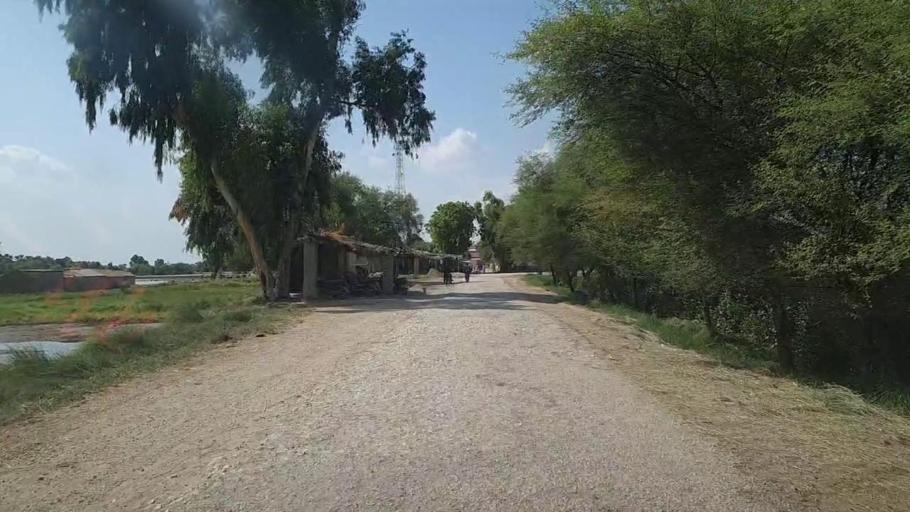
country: PK
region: Sindh
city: Khairpur
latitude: 28.1188
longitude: 69.6163
